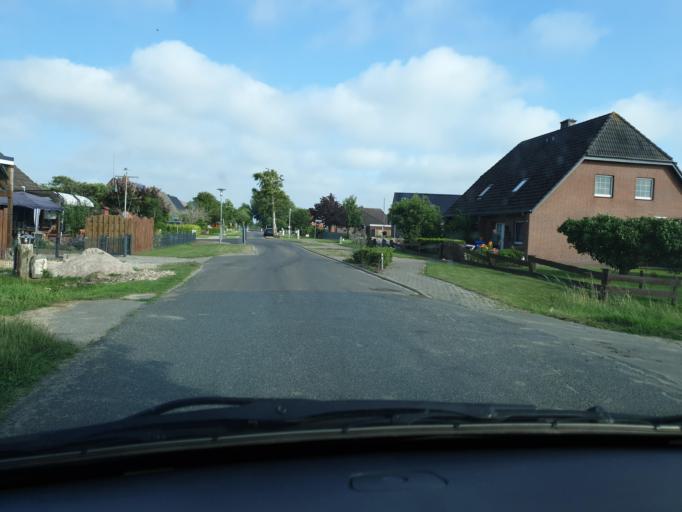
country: DE
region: Schleswig-Holstein
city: Friedrichskoog
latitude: 54.0057
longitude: 8.8726
